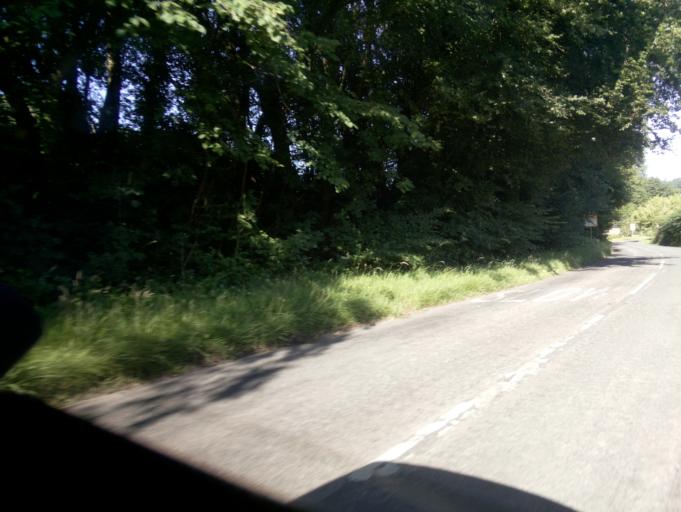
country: GB
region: England
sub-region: Gloucestershire
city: Coleford
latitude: 51.7803
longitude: -2.6425
